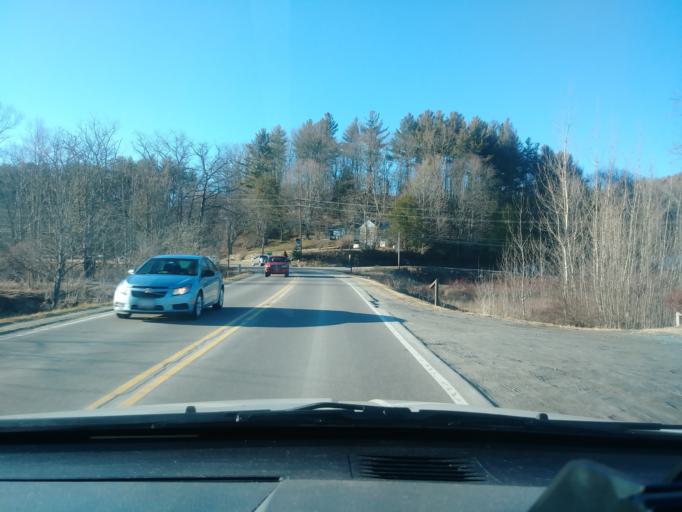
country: US
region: North Carolina
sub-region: Avery County
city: Banner Elk
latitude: 36.1526
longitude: -81.8626
